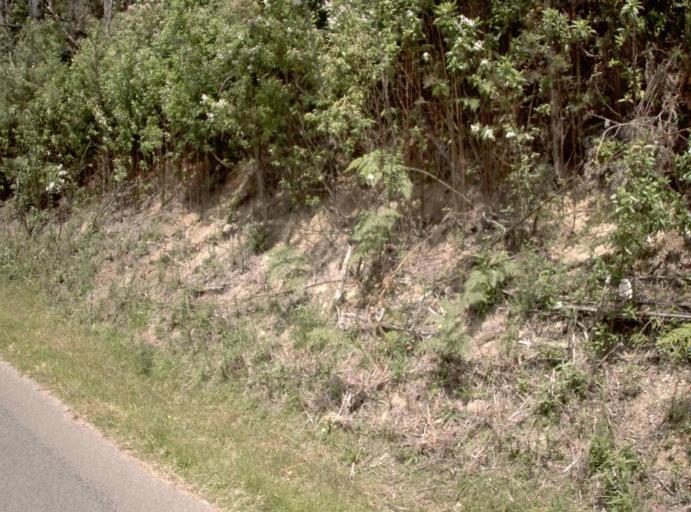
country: AU
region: Victoria
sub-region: Latrobe
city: Traralgon
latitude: -38.4301
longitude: 146.5597
